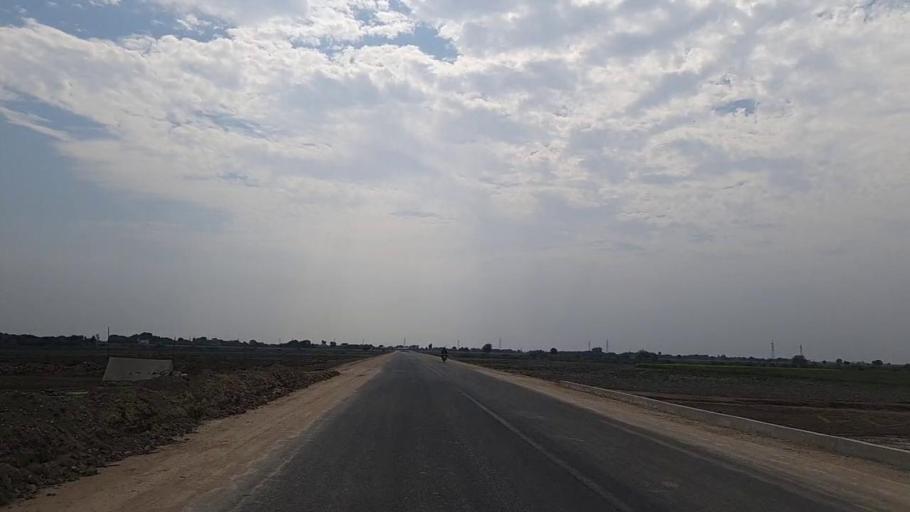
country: PK
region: Sindh
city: Naukot
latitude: 24.9748
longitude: 69.2859
